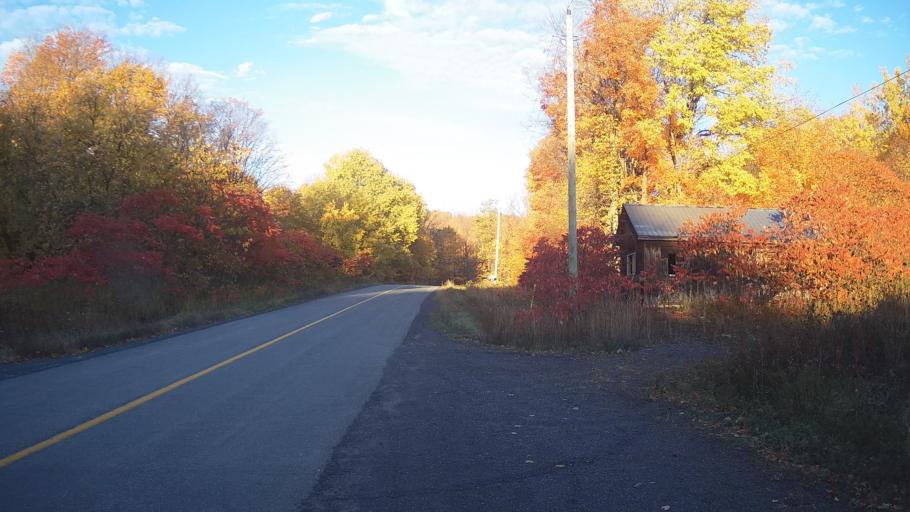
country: CA
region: Ontario
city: Arnprior
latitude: 45.3449
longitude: -76.3343
